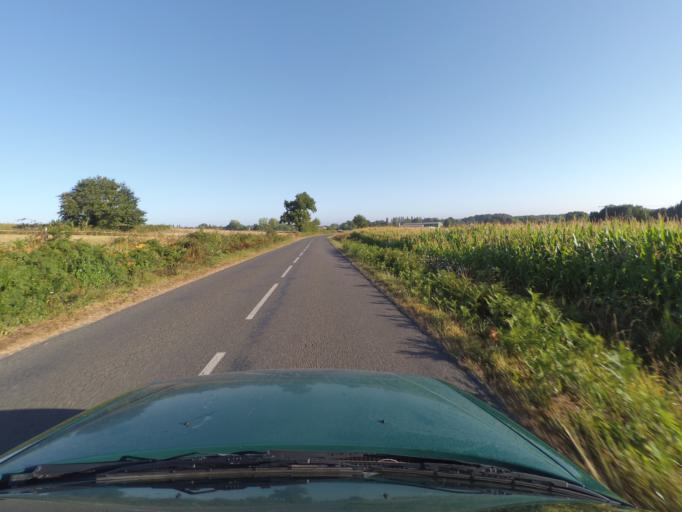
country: FR
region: Pays de la Loire
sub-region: Departement de la Loire-Atlantique
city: Montbert
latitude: 47.0469
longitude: -1.4814
